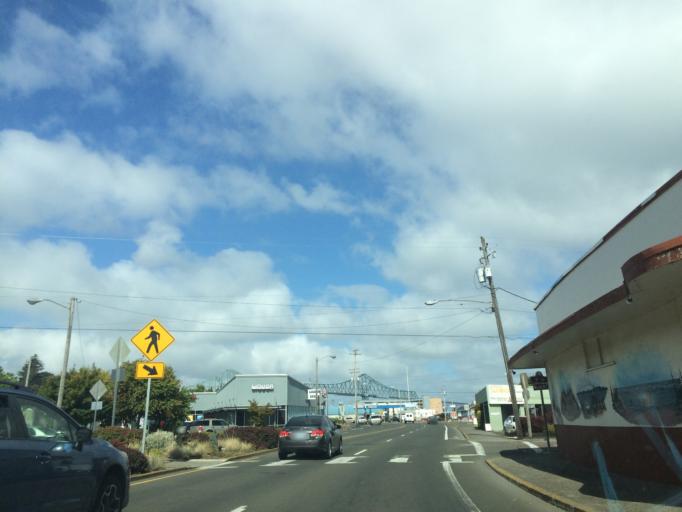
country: US
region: Oregon
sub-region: Clatsop County
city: Astoria
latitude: 46.1899
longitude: -123.8343
